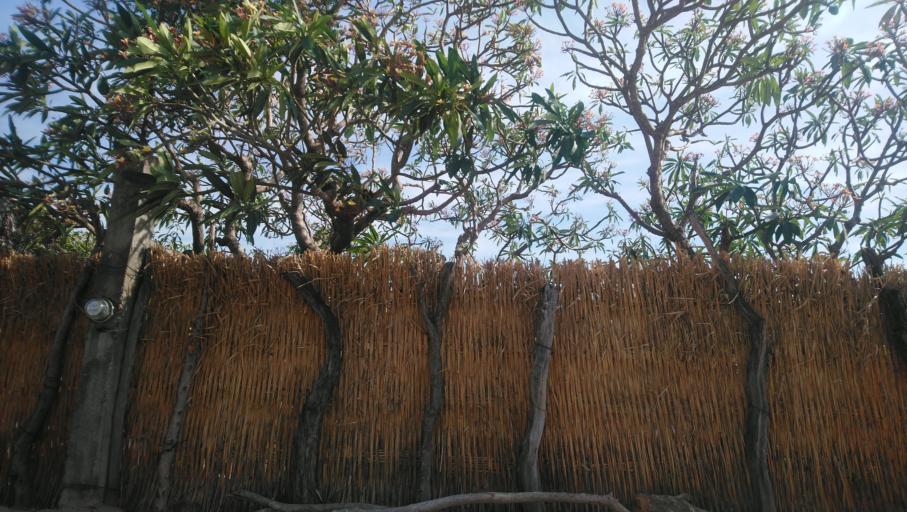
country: MX
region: Oaxaca
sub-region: Salina Cruz
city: Salina Cruz
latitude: 16.2200
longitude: -95.1253
